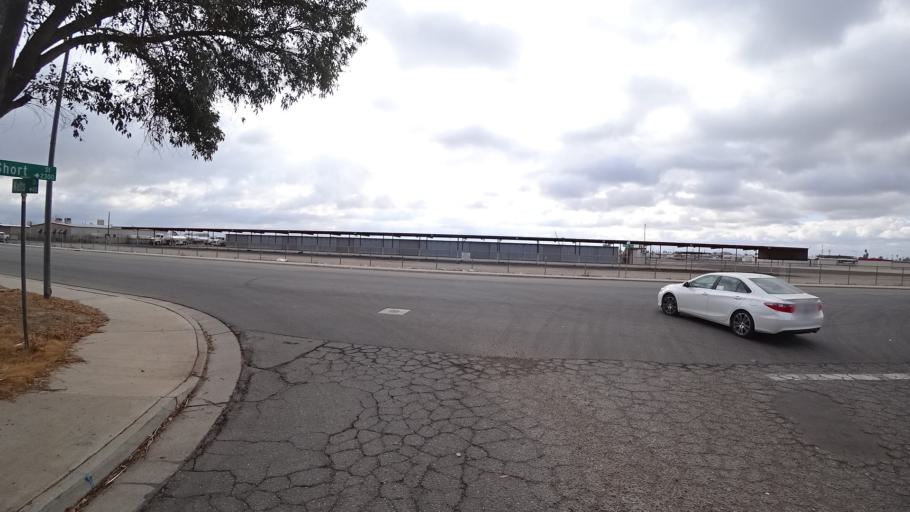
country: US
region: California
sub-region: Kern County
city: Bakersfield
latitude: 35.3323
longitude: -118.9995
